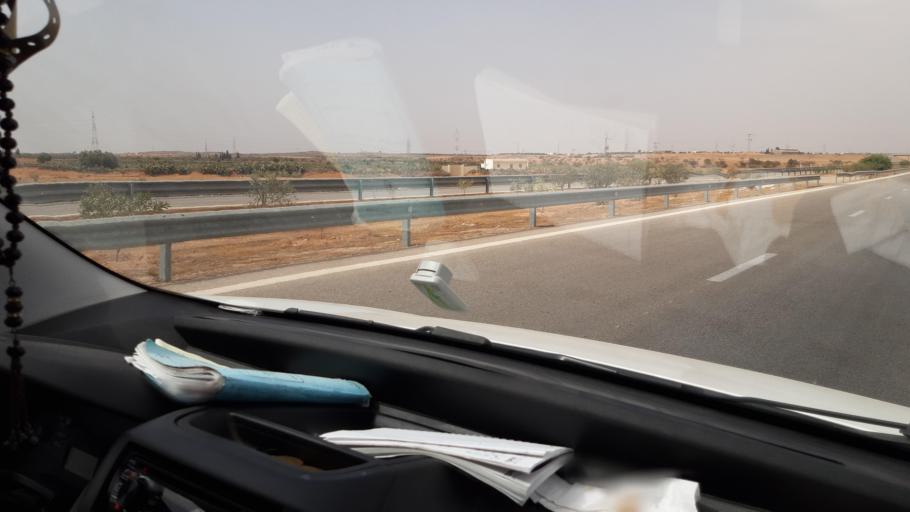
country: TN
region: Safaqis
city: Sfax
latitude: 34.7764
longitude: 10.6119
